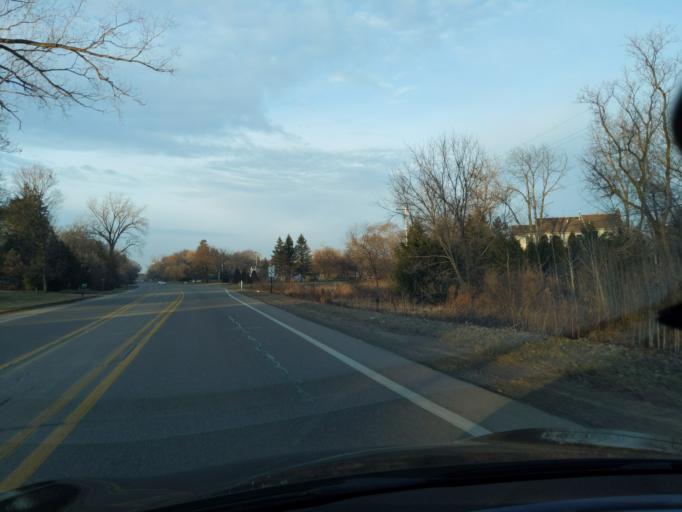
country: US
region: Michigan
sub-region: Livingston County
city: Brighton
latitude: 42.5692
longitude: -83.7528
